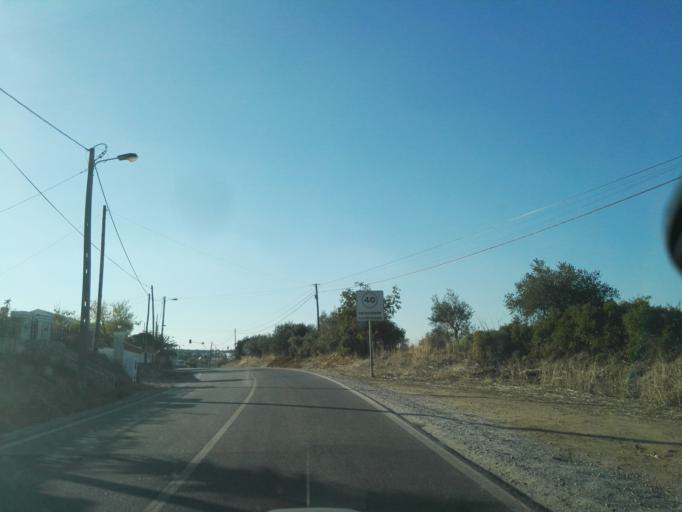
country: PT
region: Portalegre
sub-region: Elvas
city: Elvas
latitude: 38.8811
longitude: -7.1989
